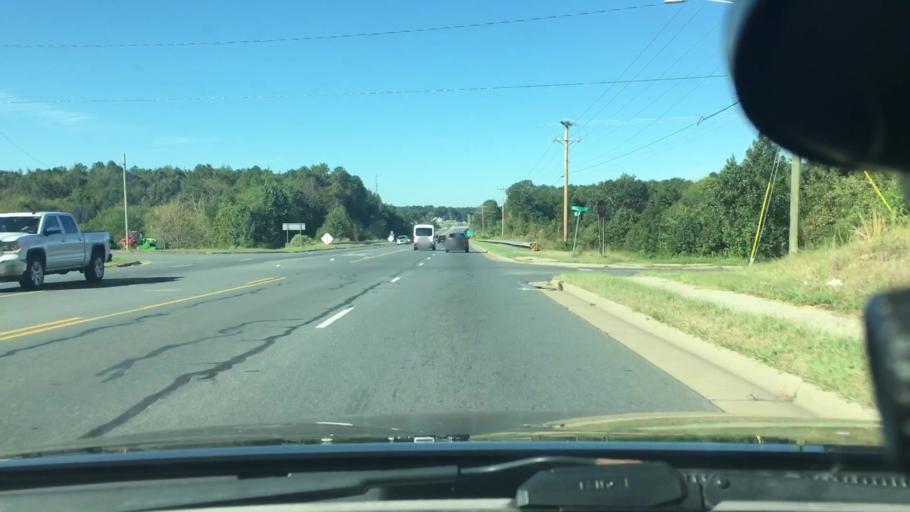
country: US
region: North Carolina
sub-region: Stanly County
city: Albemarle
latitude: 35.3417
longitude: -80.1860
